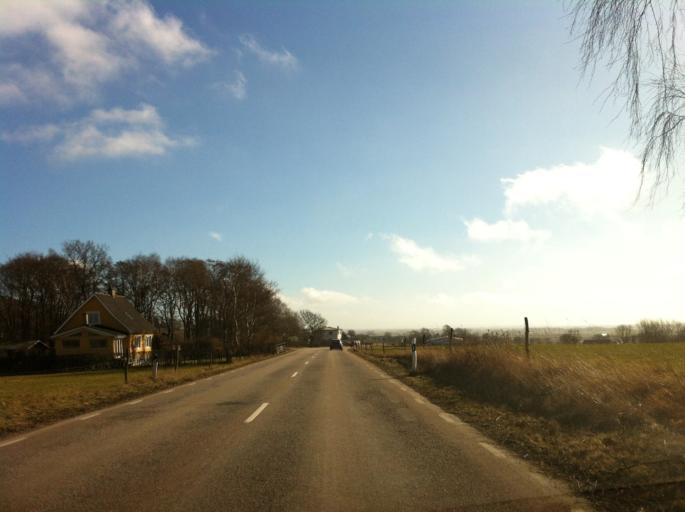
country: SE
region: Skane
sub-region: Bastads Kommun
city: Forslov
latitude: 56.3409
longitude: 12.8236
